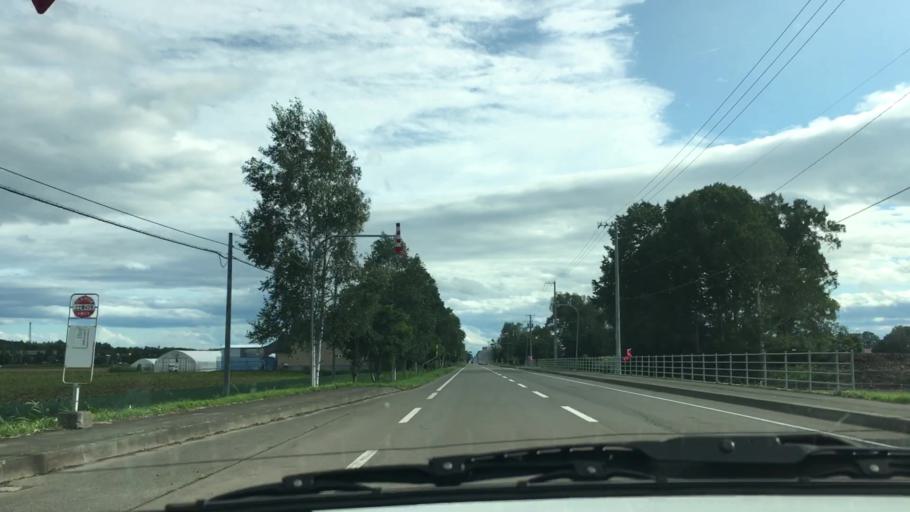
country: JP
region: Hokkaido
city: Otofuke
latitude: 43.2442
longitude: 143.2976
